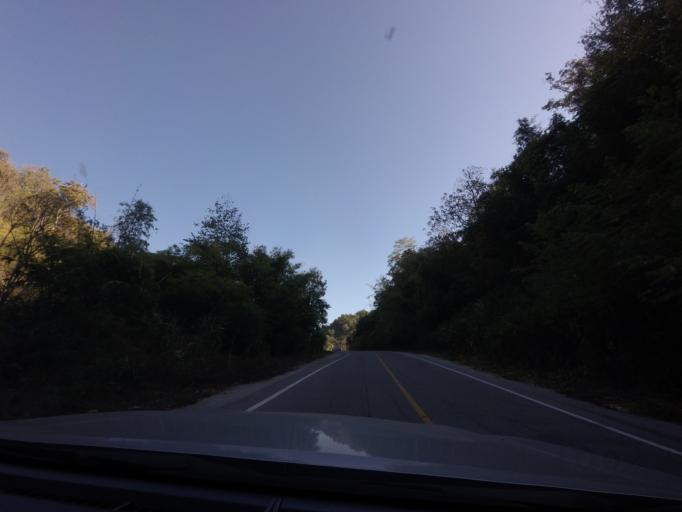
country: TH
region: Lampang
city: Chae Hom
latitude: 18.5593
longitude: 99.6268
